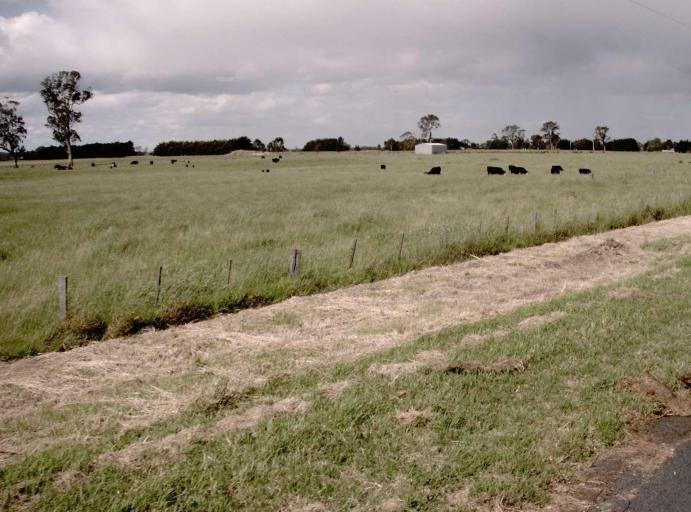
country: AU
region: Victoria
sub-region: Latrobe
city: Traralgon
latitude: -38.1525
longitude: 146.5076
